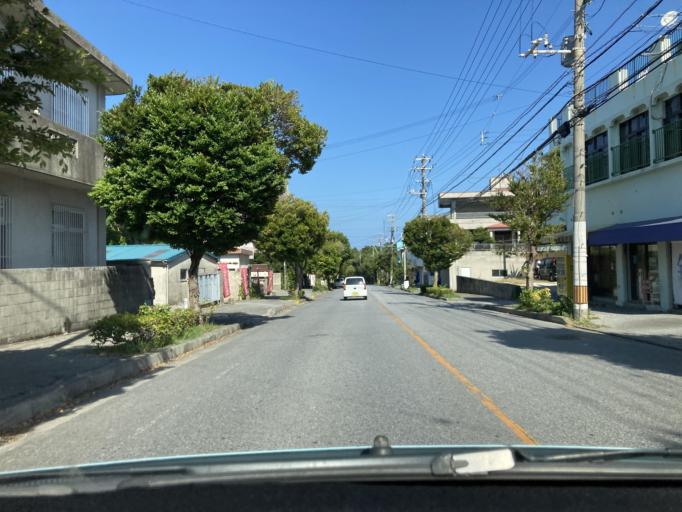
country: JP
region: Okinawa
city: Ginowan
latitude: 26.2505
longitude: 127.7263
